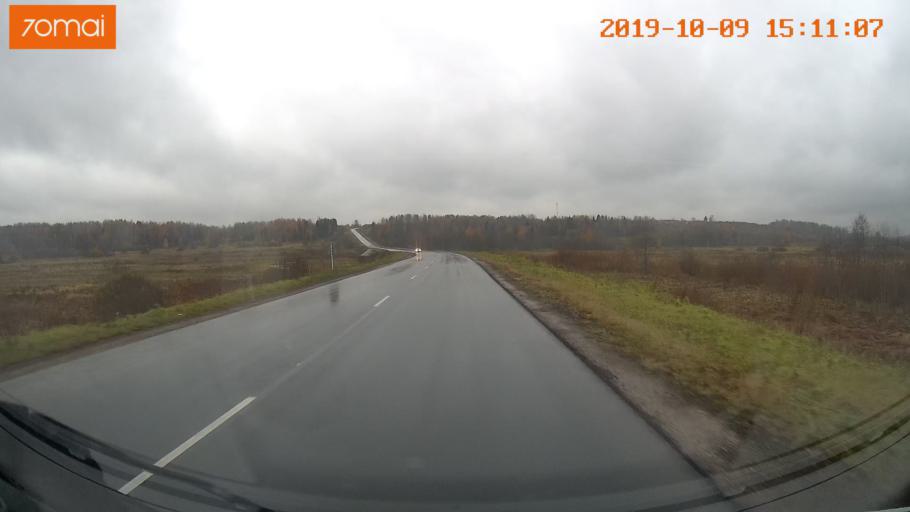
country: RU
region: Kostroma
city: Susanino
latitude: 58.1694
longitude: 41.6321
